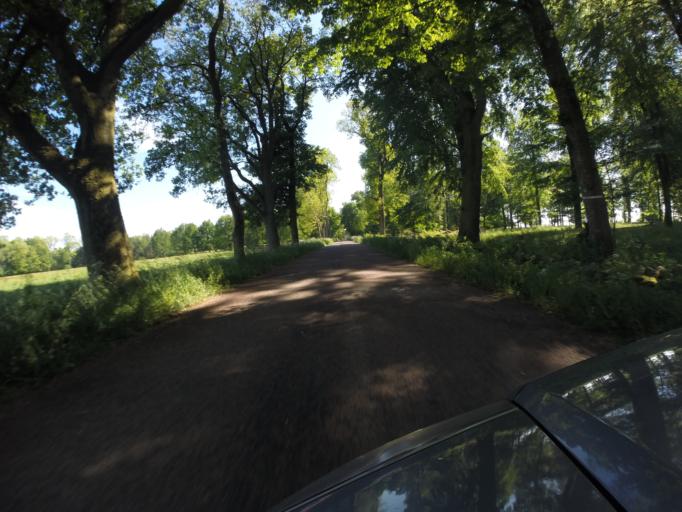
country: SE
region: Skane
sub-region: Helsingborg
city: Hyllinge
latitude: 56.0938
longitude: 12.8300
